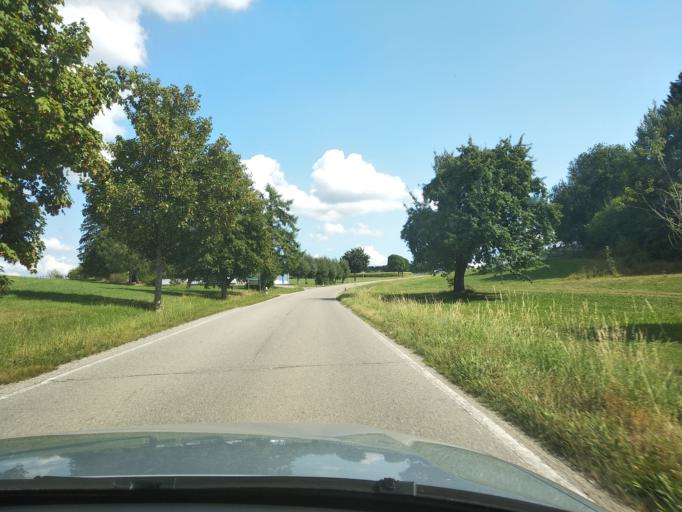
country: DE
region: Baden-Wuerttemberg
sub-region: Tuebingen Region
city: Leutkirch im Allgau
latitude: 47.8884
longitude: 9.9767
